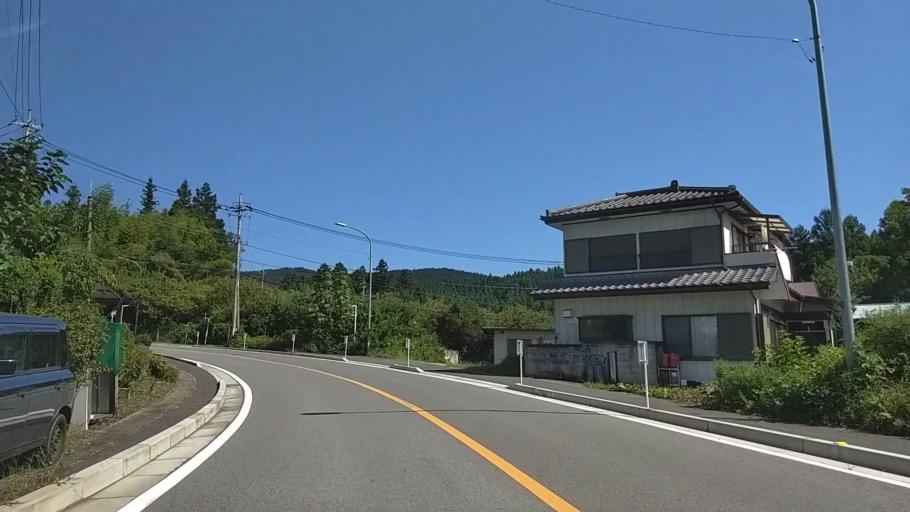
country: JP
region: Gunma
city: Annaka
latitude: 36.3396
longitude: 138.7270
